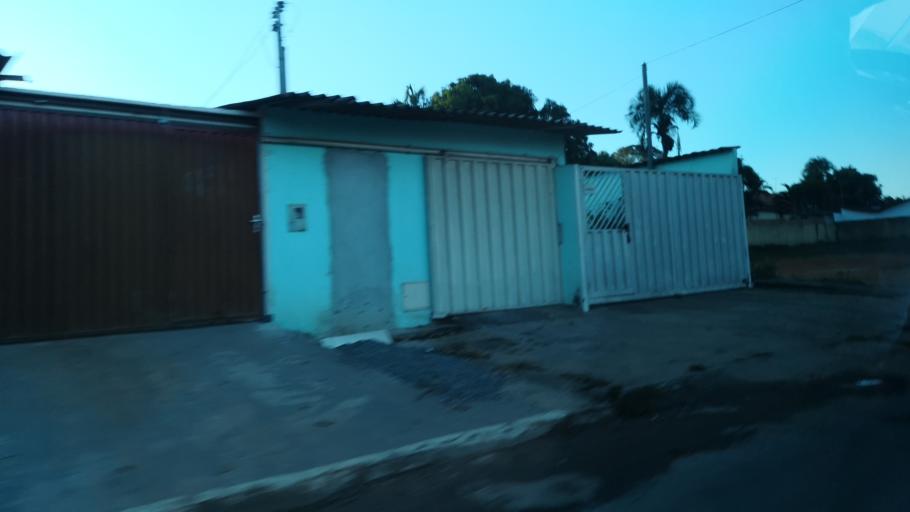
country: BR
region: Goias
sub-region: Goiania
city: Goiania
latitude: -16.6919
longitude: -49.1880
